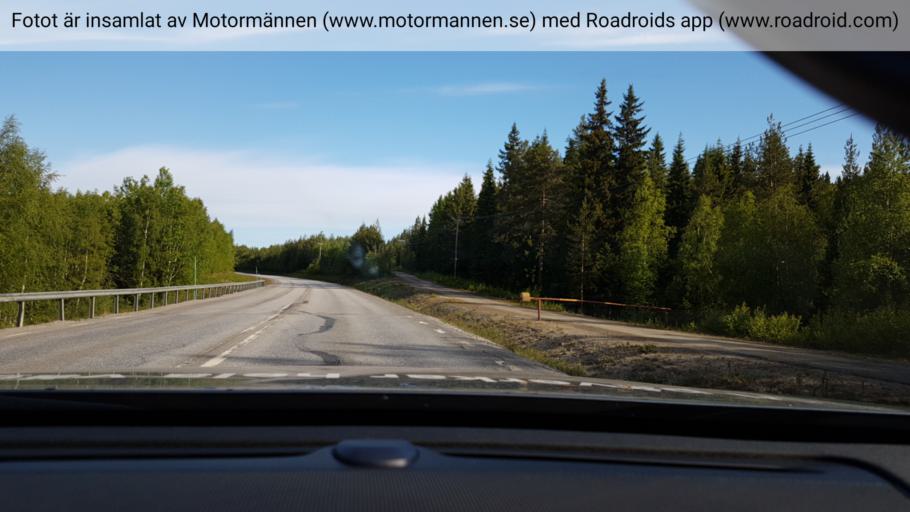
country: SE
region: Vaesterbotten
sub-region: Vannas Kommun
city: Vaennaes
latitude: 63.9418
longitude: 19.7706
